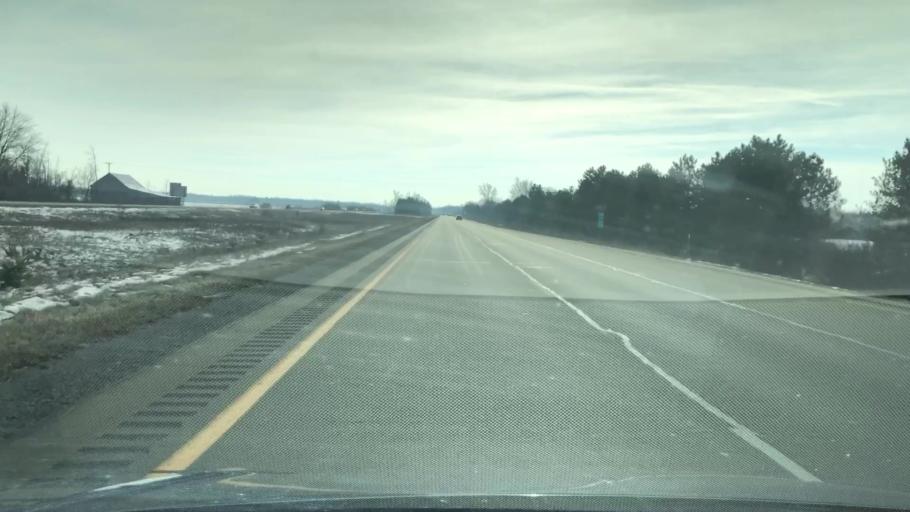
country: US
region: Michigan
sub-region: Arenac County
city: Standish
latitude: 43.9776
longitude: -84.0169
